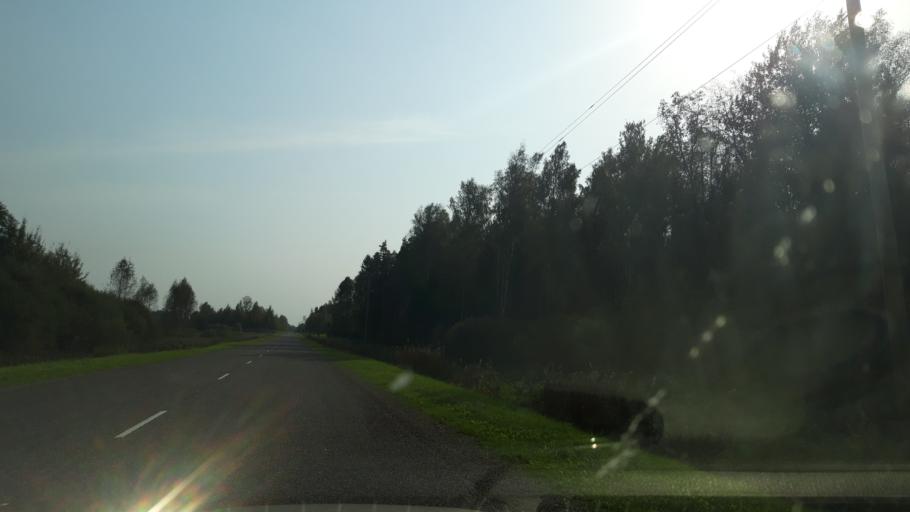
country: LV
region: Burtnieki
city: Matisi
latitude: 57.6418
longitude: 25.2482
